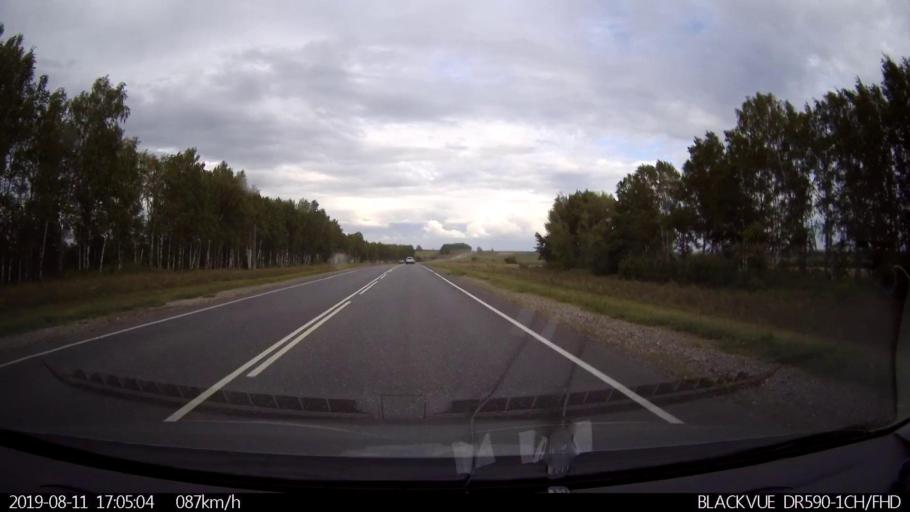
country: RU
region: Ulyanovsk
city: Mayna
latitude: 54.2994
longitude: 47.7781
